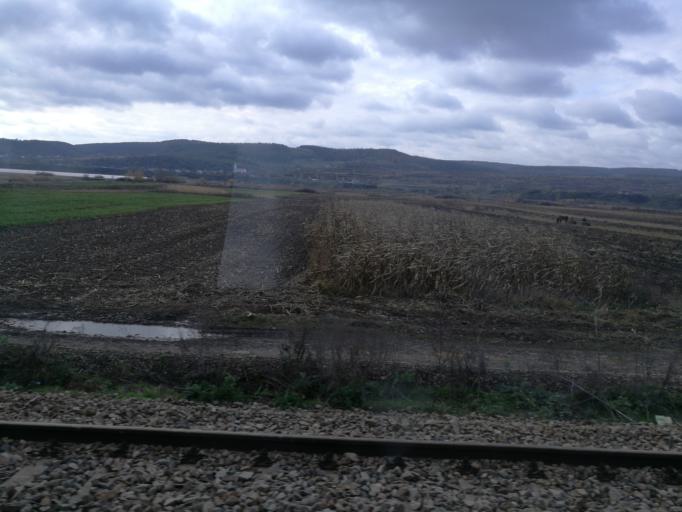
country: RO
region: Bacau
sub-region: Comuna Racaciuni
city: Gheorghe Doja
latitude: 46.3991
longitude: 26.9620
